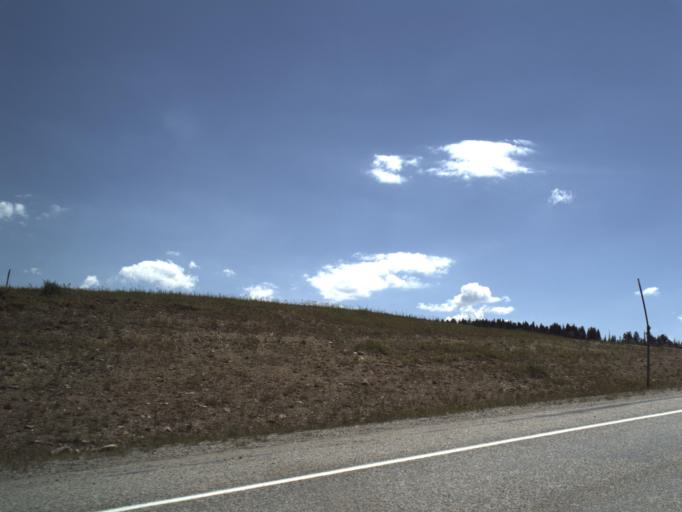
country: US
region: Utah
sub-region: Rich County
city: Randolph
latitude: 41.4730
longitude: -111.4730
